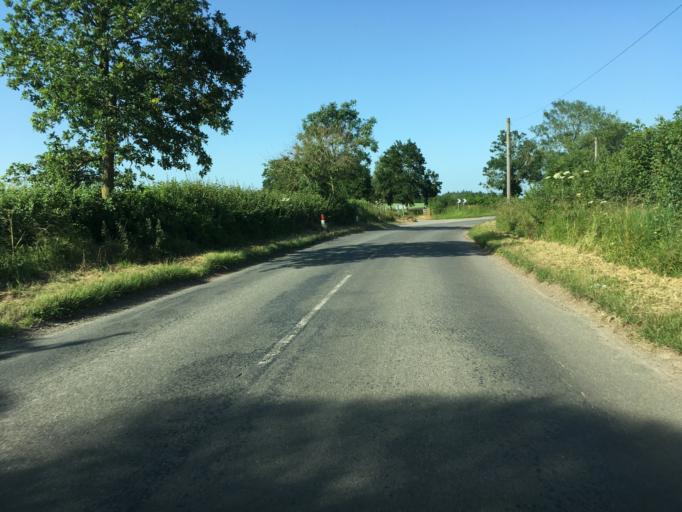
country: GB
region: England
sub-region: Buckinghamshire
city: Steeple Claydon
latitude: 51.9287
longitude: -1.0510
